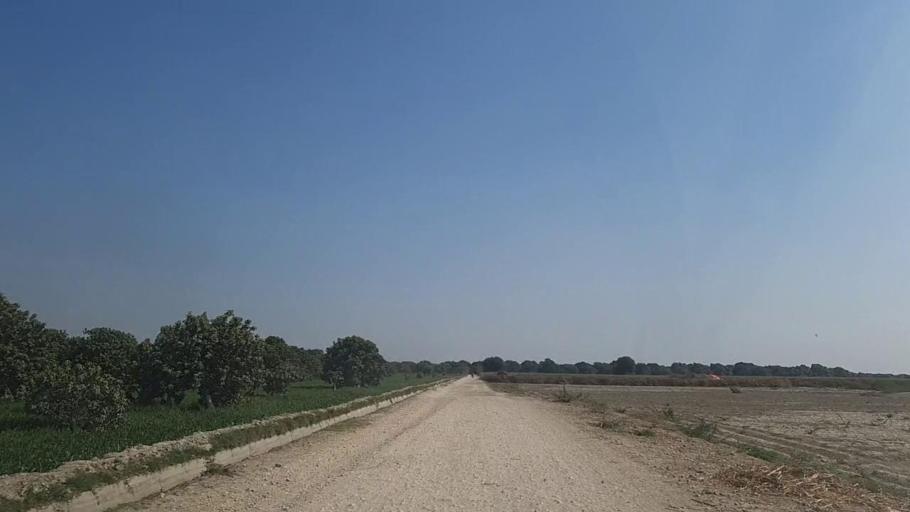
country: PK
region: Sindh
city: Digri
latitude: 25.1691
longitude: 69.2063
